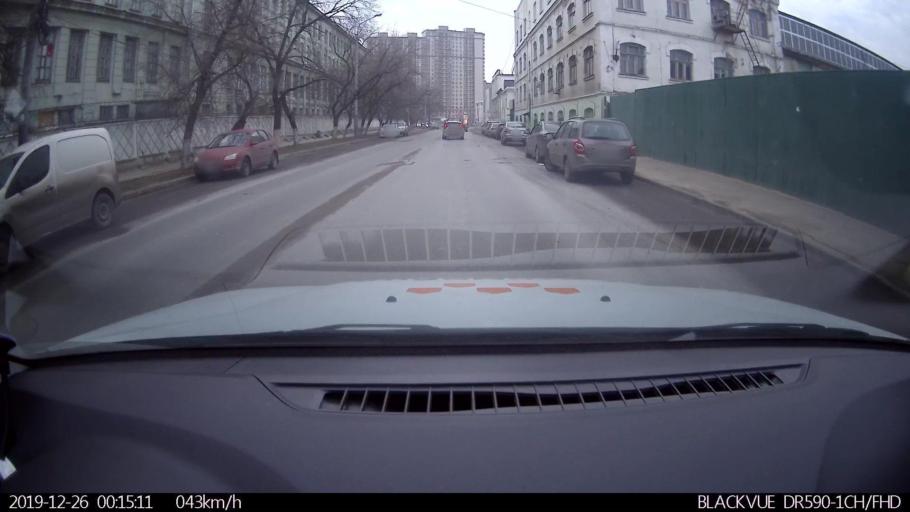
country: RU
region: Nizjnij Novgorod
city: Nizhniy Novgorod
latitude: 56.3117
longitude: 43.9489
